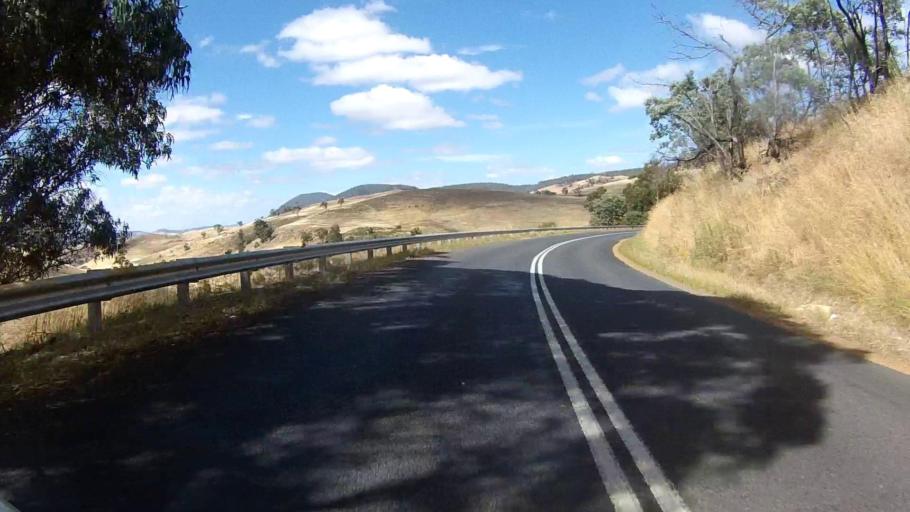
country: AU
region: Tasmania
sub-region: Brighton
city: Bridgewater
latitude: -42.5647
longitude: 147.3913
